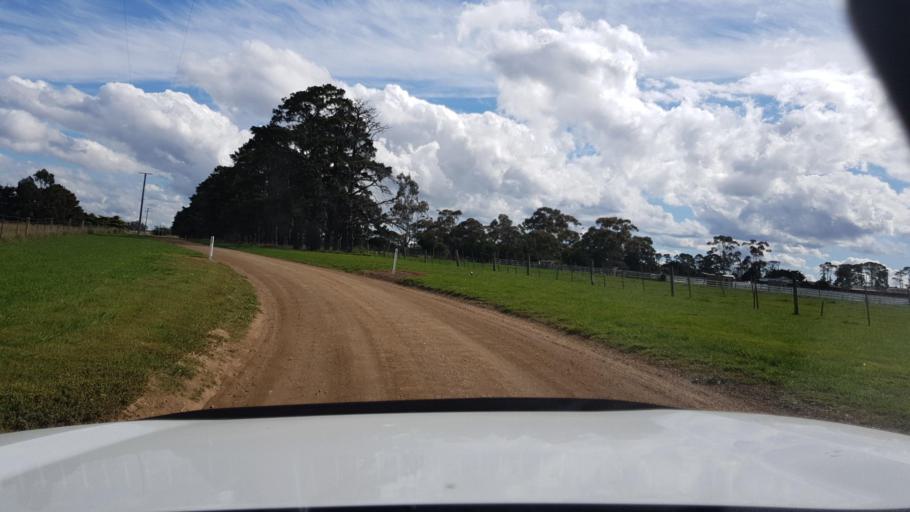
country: AU
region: Victoria
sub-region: Hume
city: Sunbury
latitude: -37.5852
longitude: 144.6633
